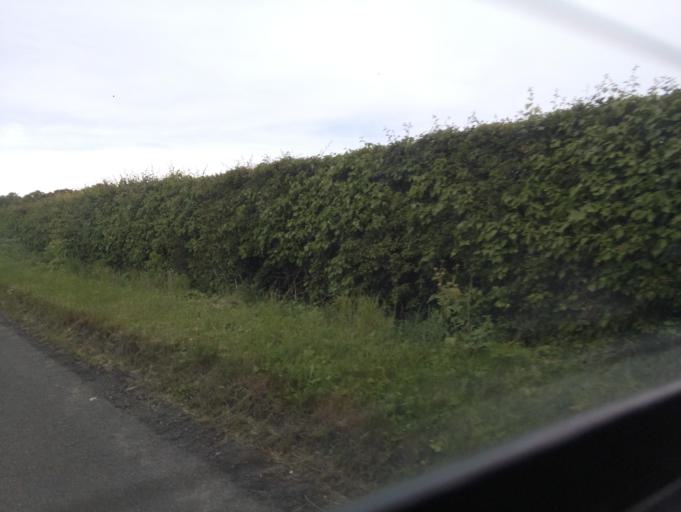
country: GB
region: Scotland
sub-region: East Lothian
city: Musselburgh
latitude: 55.9116
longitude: -3.0063
